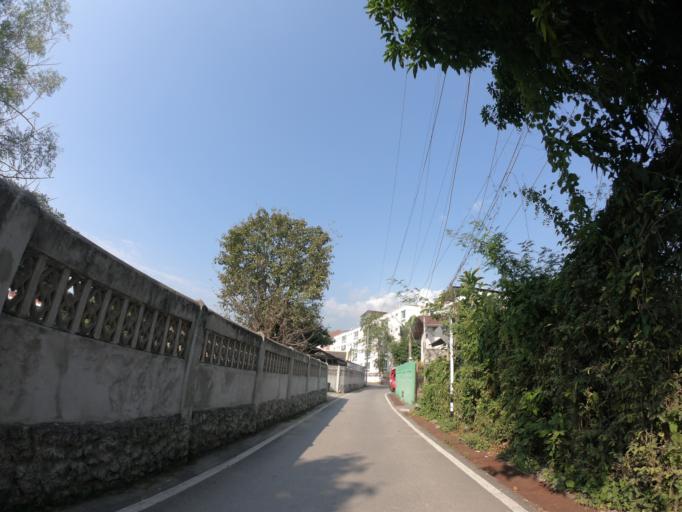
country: TH
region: Chiang Mai
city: Chiang Mai
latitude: 18.7819
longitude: 98.9557
